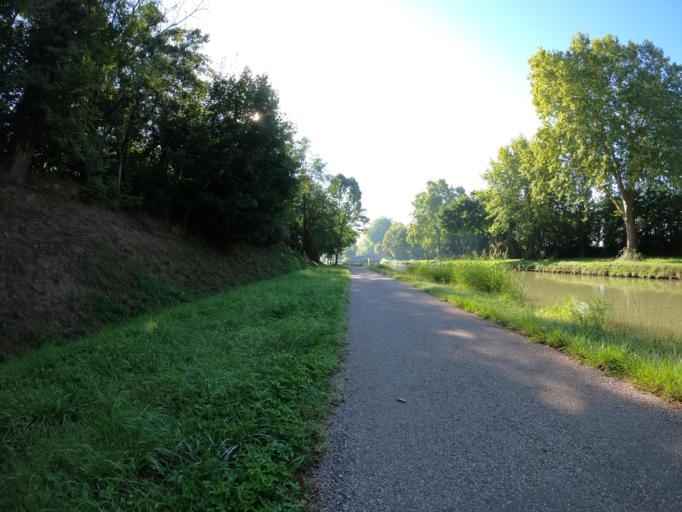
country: FR
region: Midi-Pyrenees
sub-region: Departement du Tarn-et-Garonne
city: Montech
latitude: 43.9801
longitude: 1.2151
